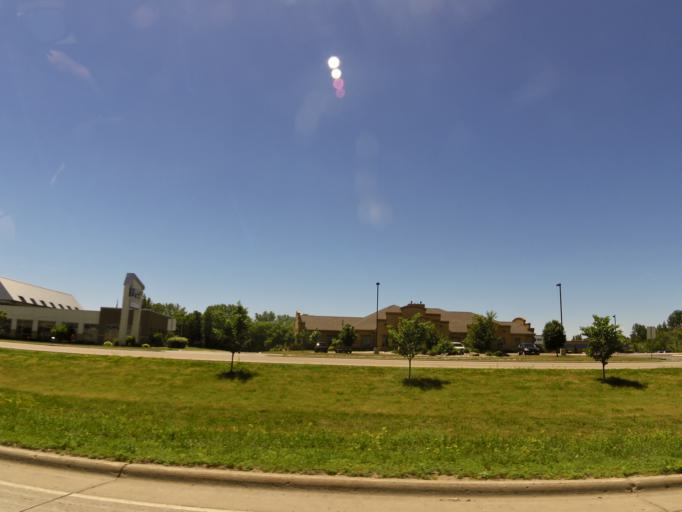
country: US
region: Minnesota
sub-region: Becker County
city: Detroit Lakes
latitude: 46.8126
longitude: -95.8302
